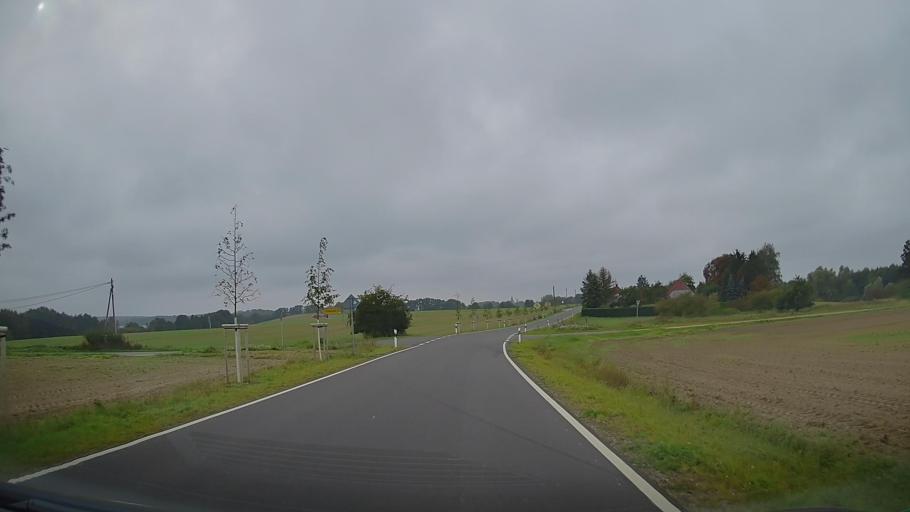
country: DE
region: Mecklenburg-Vorpommern
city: Kavelstorf
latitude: 53.9305
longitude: 12.2058
